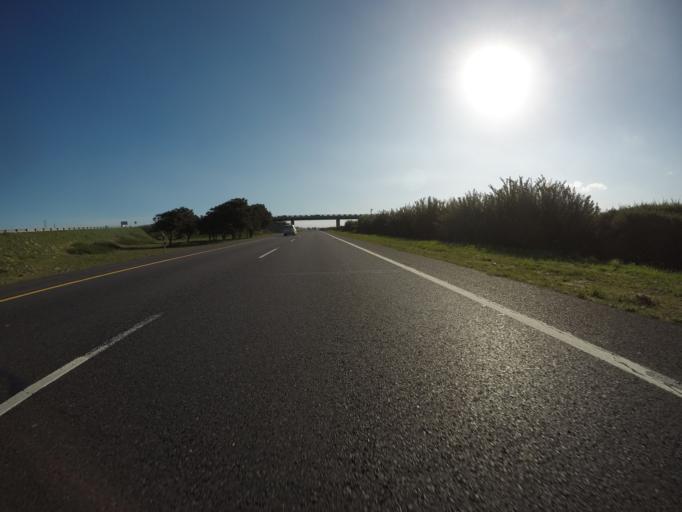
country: ZA
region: Western Cape
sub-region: Cape Winelands District Municipality
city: Stellenbosch
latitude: -34.0400
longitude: 18.7250
